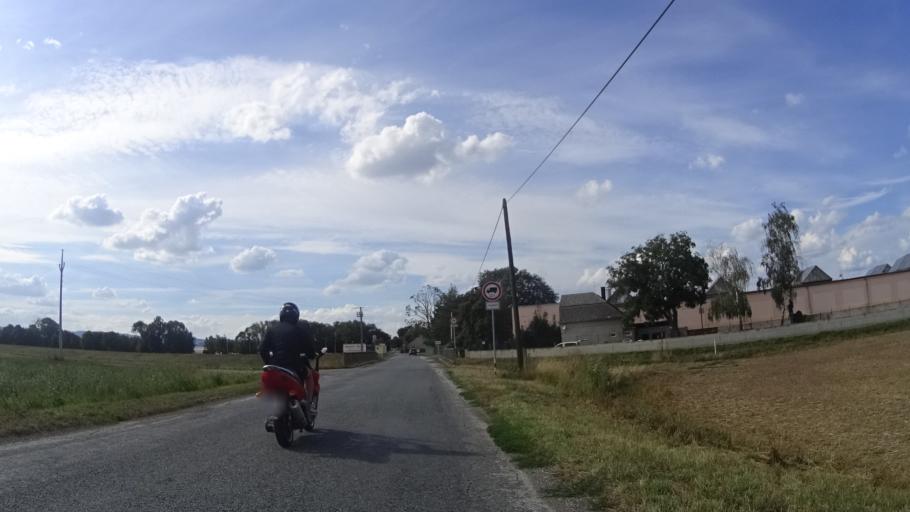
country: CZ
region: Olomoucky
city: Moravicany
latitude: 49.7522
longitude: 16.9670
